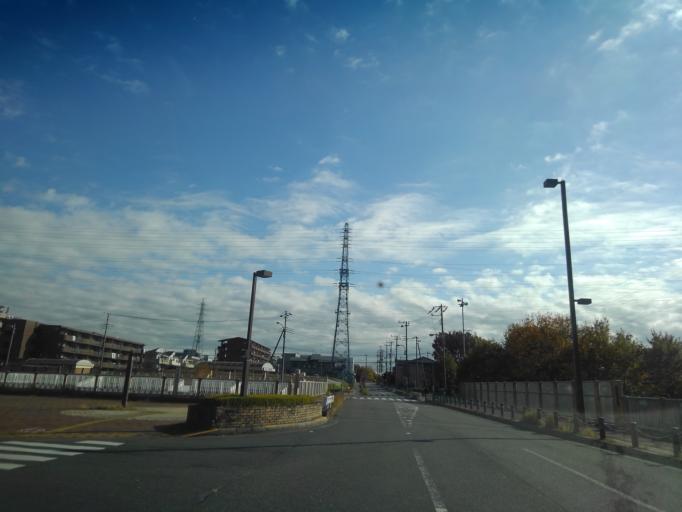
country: JP
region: Tokyo
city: Hachioji
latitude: 35.6018
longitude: 139.3665
